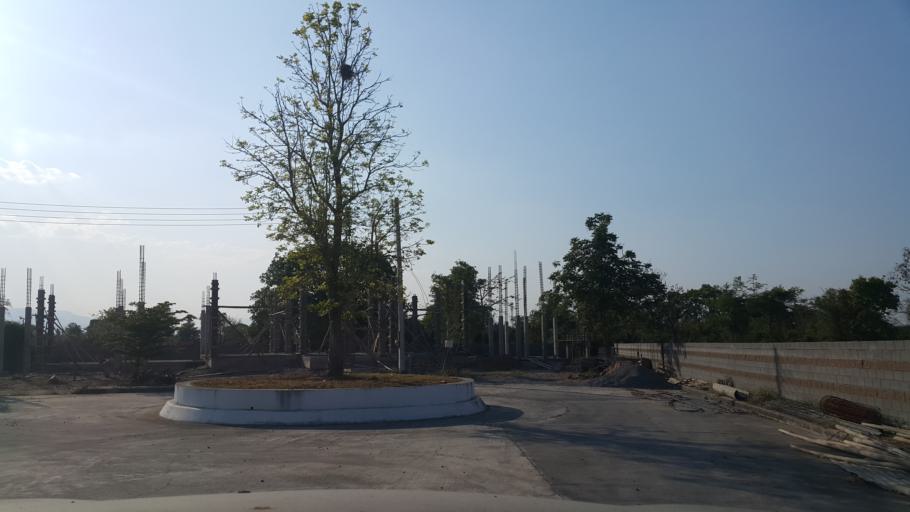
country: TH
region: Chiang Mai
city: San Sai
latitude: 18.8367
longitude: 99.1000
